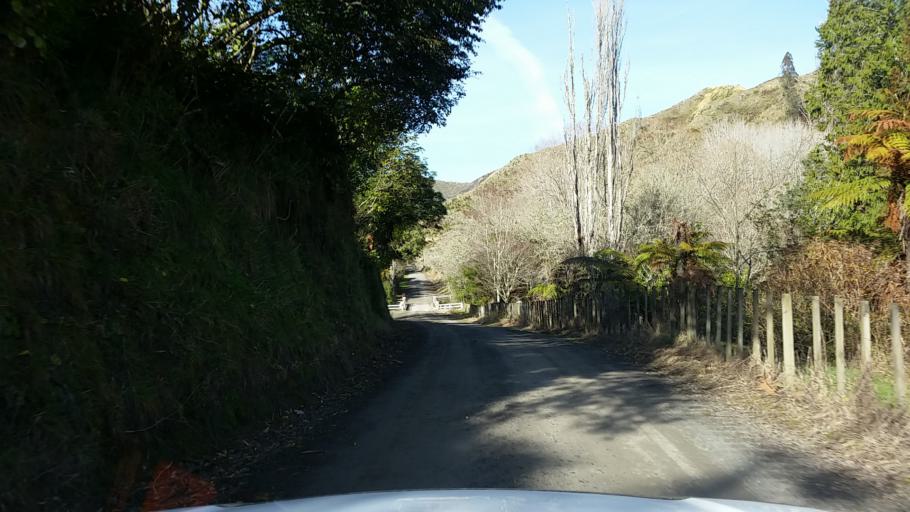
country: NZ
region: Taranaki
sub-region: South Taranaki District
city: Eltham
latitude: -39.3581
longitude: 174.5122
